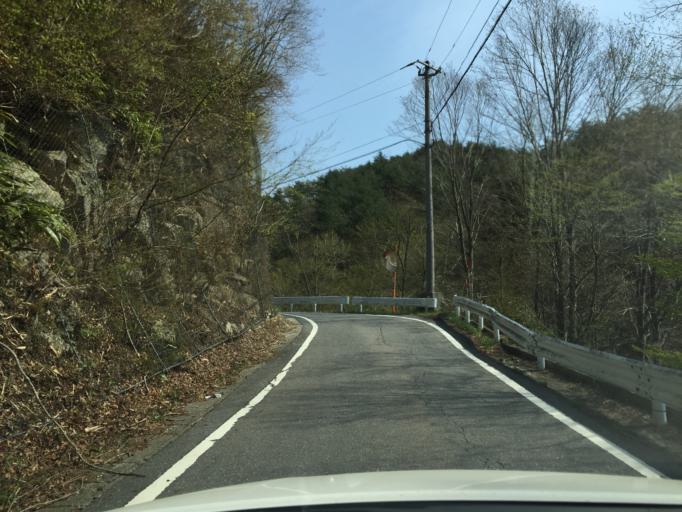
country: JP
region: Fukushima
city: Iwaki
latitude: 37.2252
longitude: 140.8432
